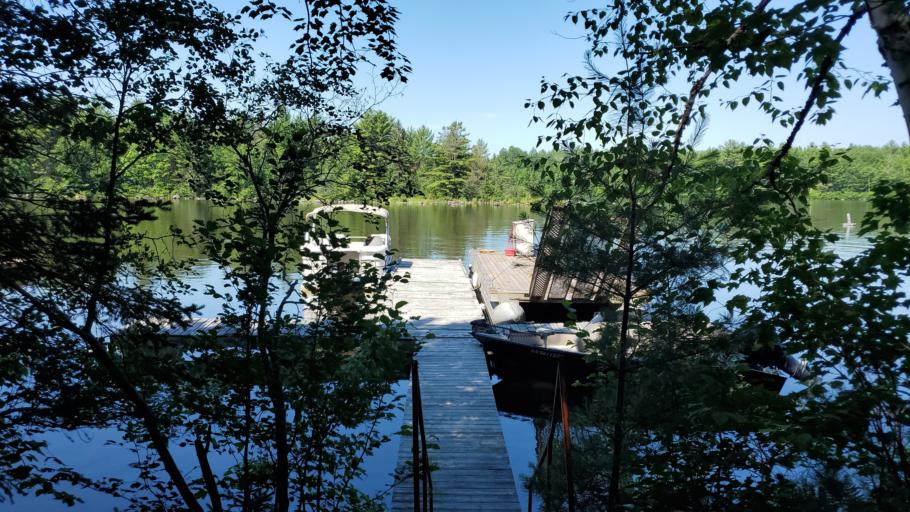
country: CA
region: Ontario
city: Mattawa
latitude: 46.2589
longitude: -78.2763
